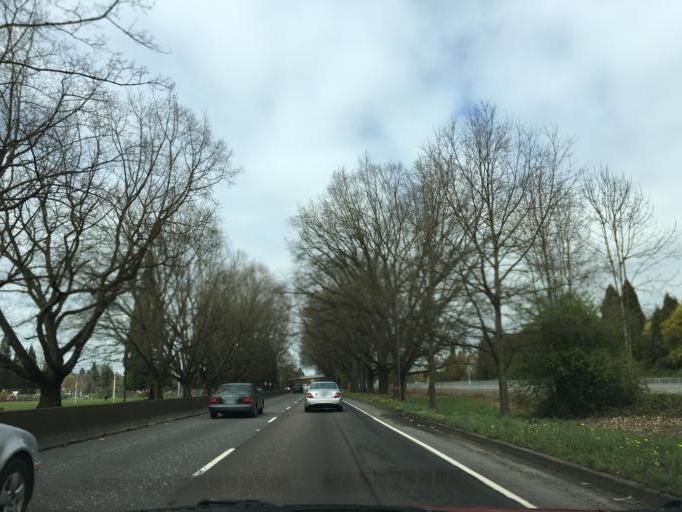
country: US
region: Oregon
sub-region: Clackamas County
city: Milwaukie
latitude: 45.4706
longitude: -122.6395
